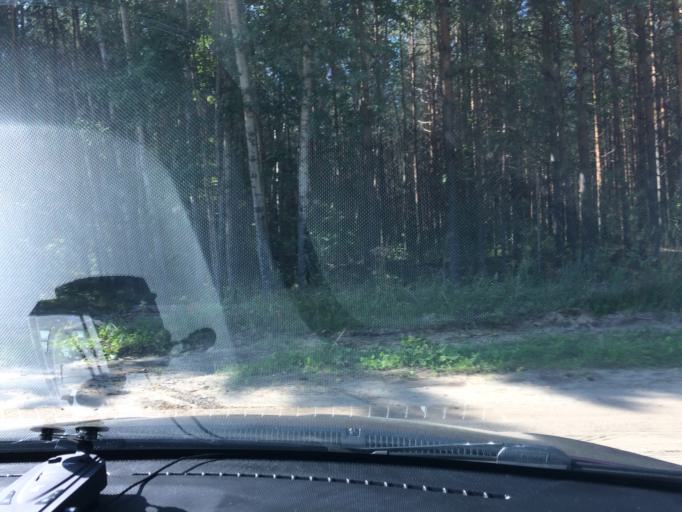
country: RU
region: Mariy-El
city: Sovetskiy
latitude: 56.5754
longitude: 48.4294
